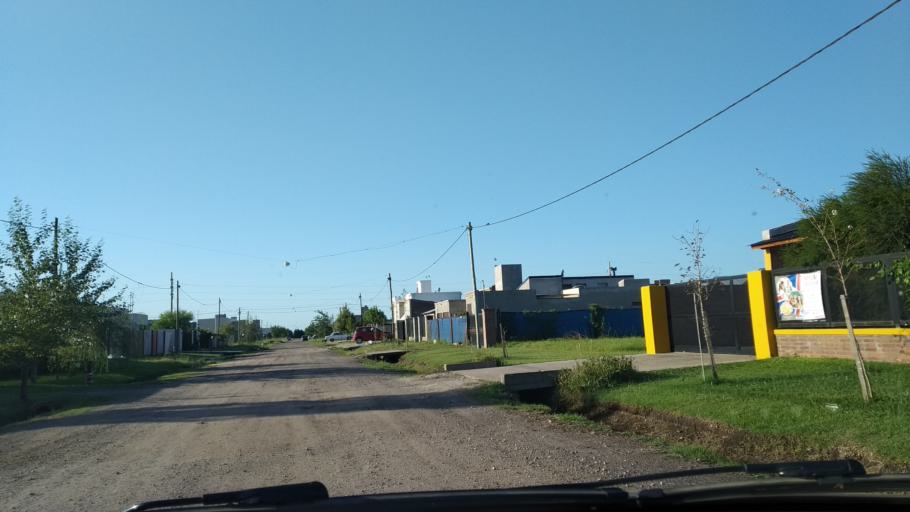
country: AR
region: Santa Fe
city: Funes
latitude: -32.9101
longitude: -60.8007
